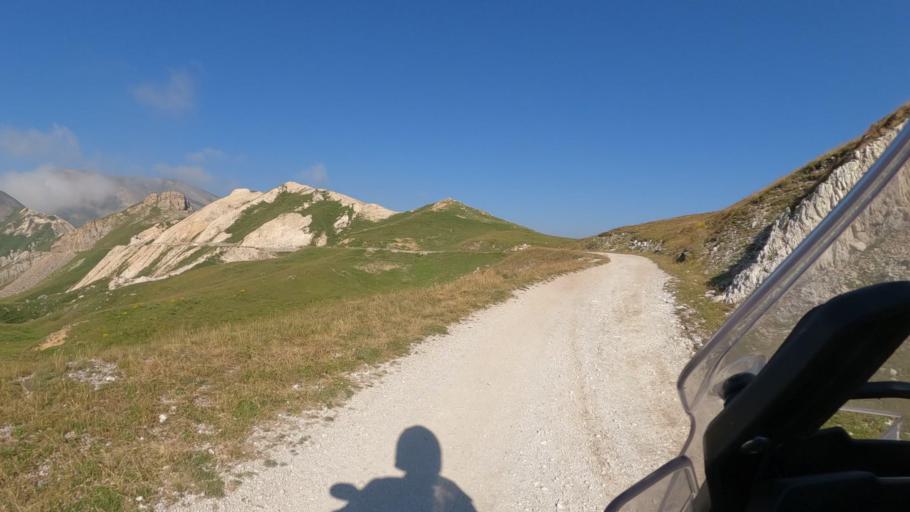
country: IT
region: Piedmont
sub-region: Provincia di Cuneo
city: Sambuco
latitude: 44.3876
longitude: 7.0692
